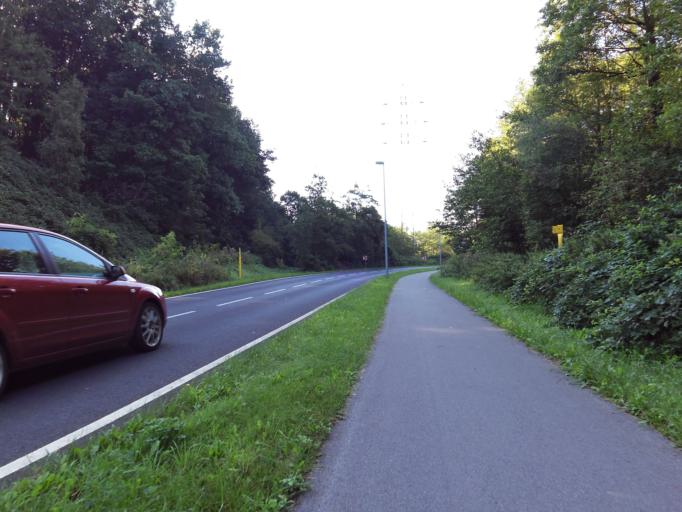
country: DE
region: North Rhine-Westphalia
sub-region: Regierungsbezirk Koln
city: Alsdorf
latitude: 50.8724
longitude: 6.1400
